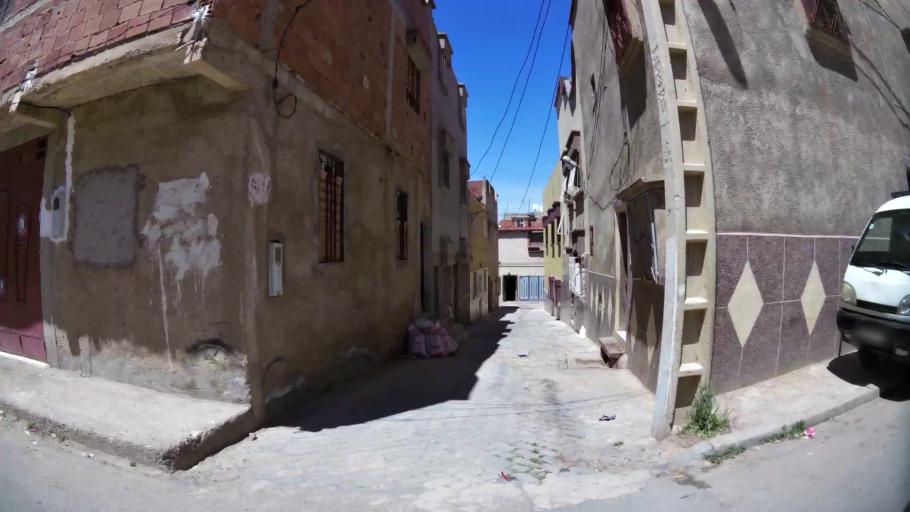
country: MA
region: Oriental
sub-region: Oujda-Angad
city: Oujda
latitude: 34.6597
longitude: -1.9276
